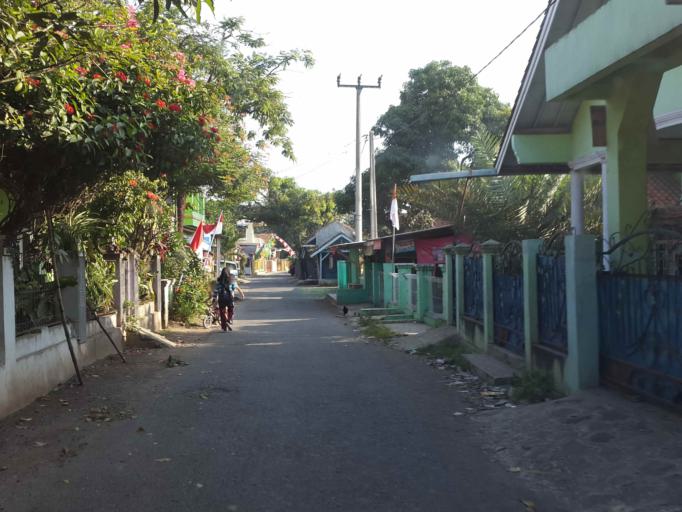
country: ID
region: West Java
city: Ciranjang-hilir
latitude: -6.8233
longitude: 107.3032
